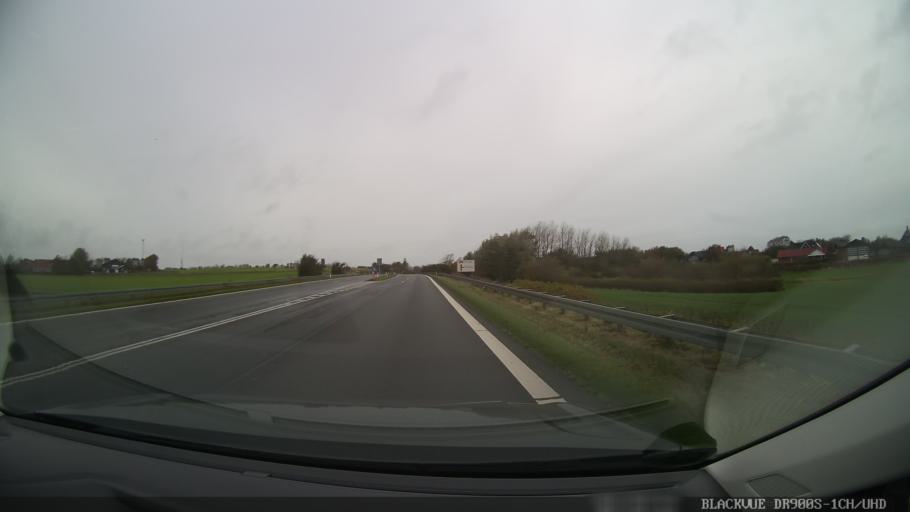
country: DK
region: North Denmark
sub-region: Thisted Kommune
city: Thisted
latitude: 56.8721
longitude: 8.6720
